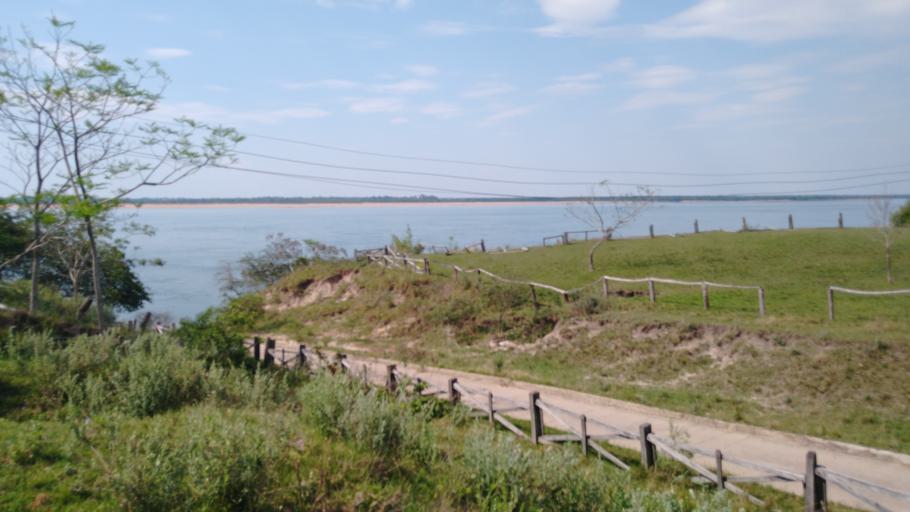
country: PY
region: Neembucu
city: Cerrito
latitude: -27.3700
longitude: -57.6553
